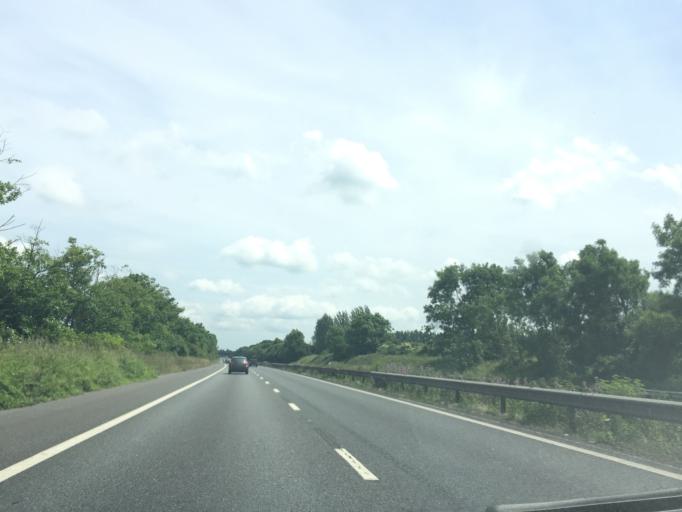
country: GB
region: England
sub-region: Kent
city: Sittingbourne
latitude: 51.3073
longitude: 0.7157
